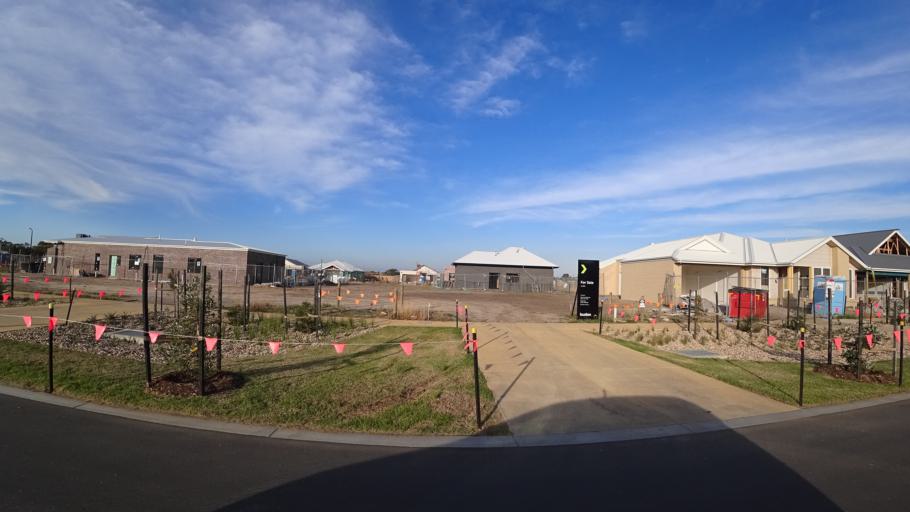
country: AU
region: Victoria
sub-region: Queenscliffe
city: Queenscliff
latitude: -38.2645
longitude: 144.6116
